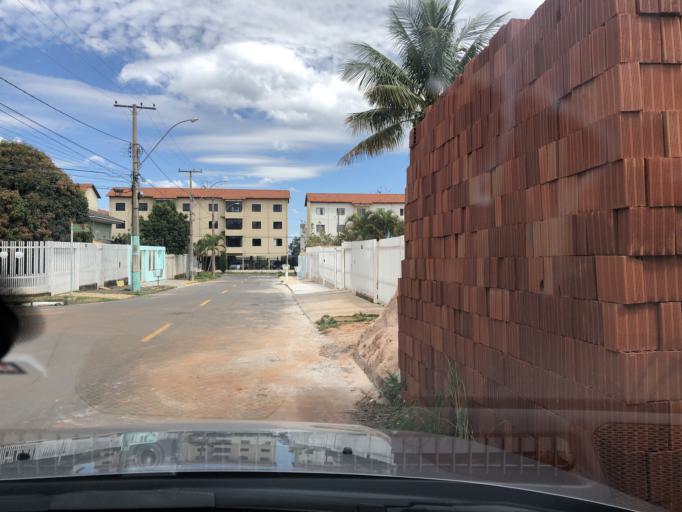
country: BR
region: Federal District
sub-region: Brasilia
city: Brasilia
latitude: -15.9956
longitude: -47.9984
